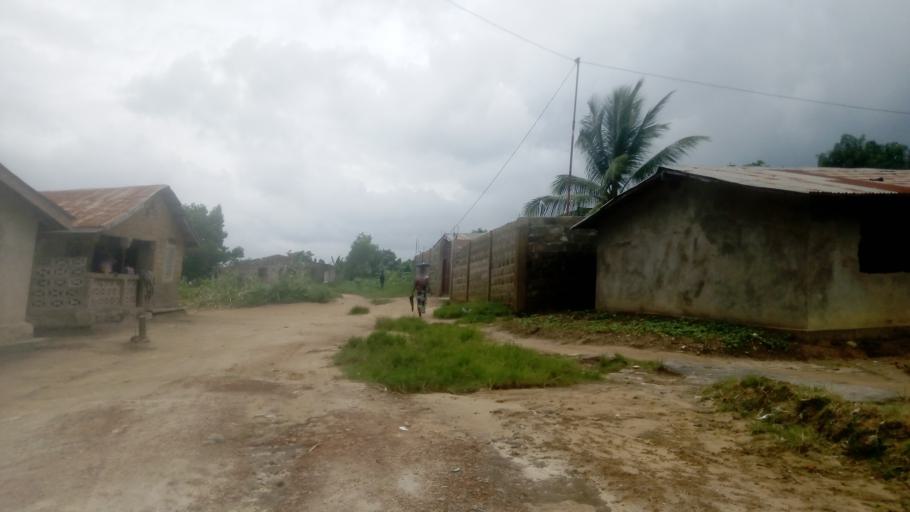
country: SL
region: Northern Province
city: Lunsar
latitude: 8.6774
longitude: -12.5394
